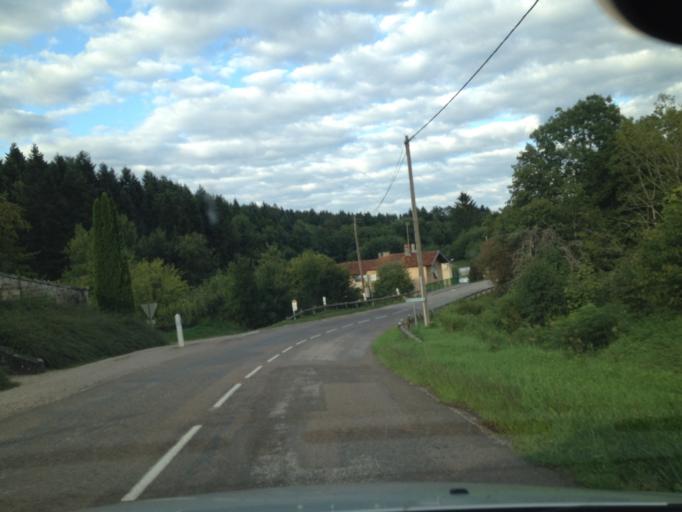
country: FR
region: Lorraine
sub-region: Departement des Vosges
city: Bains-les-Bains
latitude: 47.9766
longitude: 6.1643
